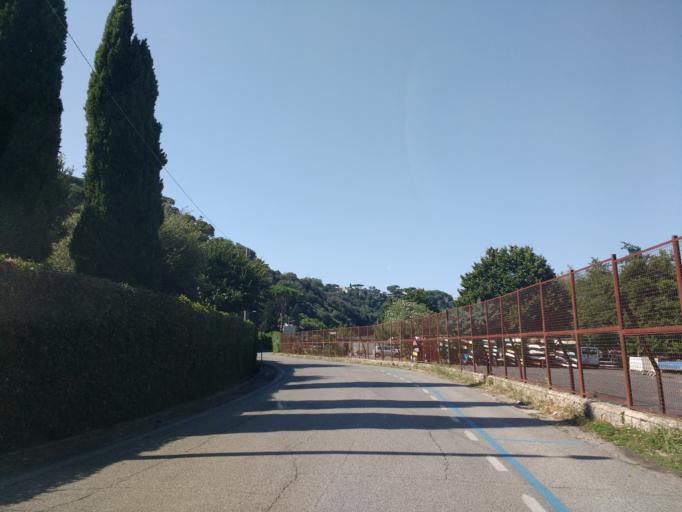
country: IT
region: Latium
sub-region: Citta metropolitana di Roma Capitale
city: Castel Gandolfo
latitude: 41.7515
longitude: 12.6517
